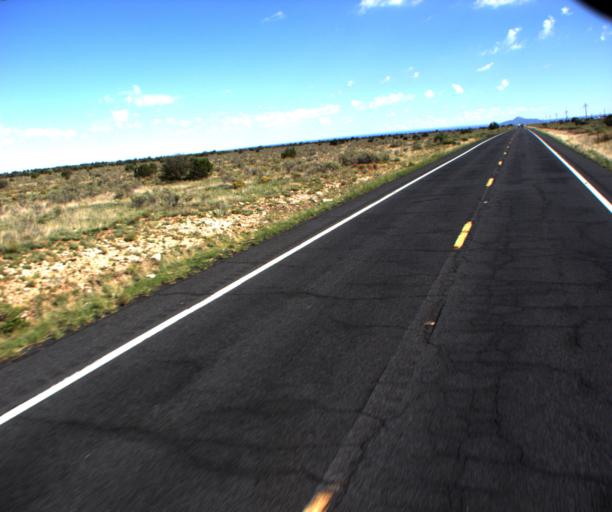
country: US
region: Arizona
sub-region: Coconino County
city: Williams
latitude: 35.5899
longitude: -112.1499
